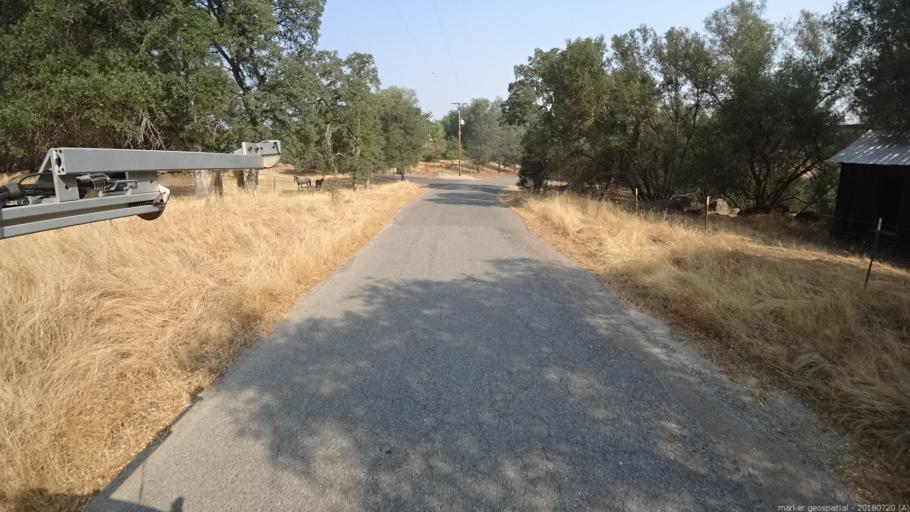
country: US
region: California
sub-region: Madera County
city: Yosemite Lakes
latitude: 37.2989
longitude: -119.8730
